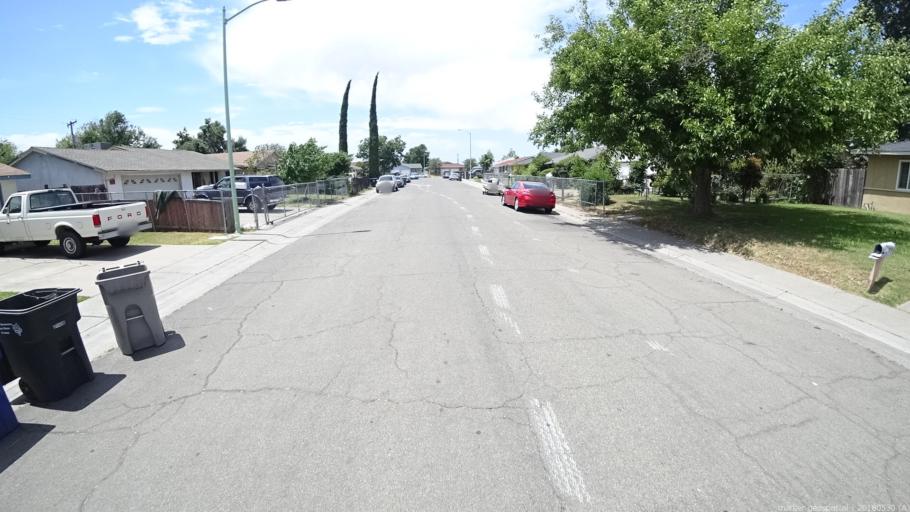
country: US
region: California
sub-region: Sacramento County
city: Sacramento
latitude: 38.6267
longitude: -121.4667
